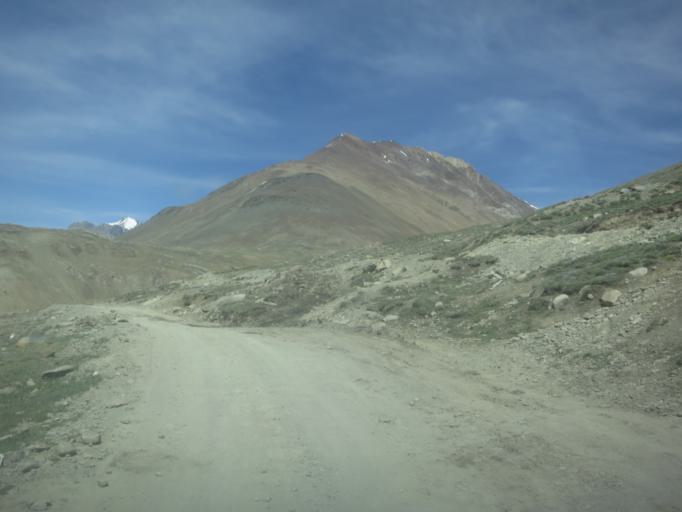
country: IN
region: Himachal Pradesh
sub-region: Kulu
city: Manali
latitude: 32.4021
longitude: 77.6415
